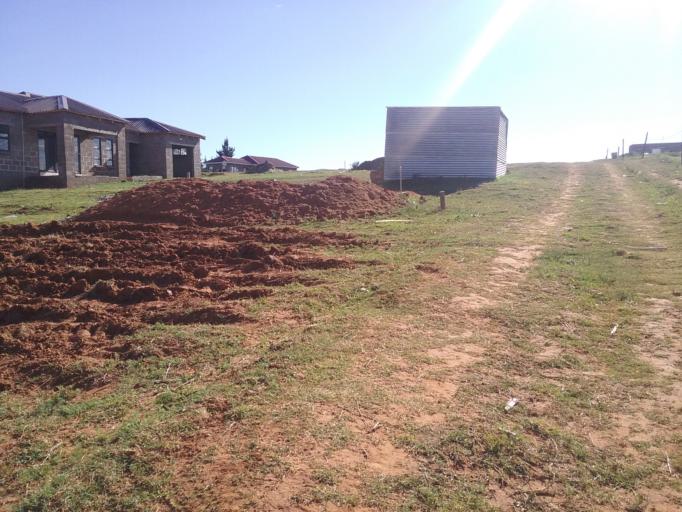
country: LS
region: Maseru
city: Maseru
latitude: -29.4237
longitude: 27.5684
